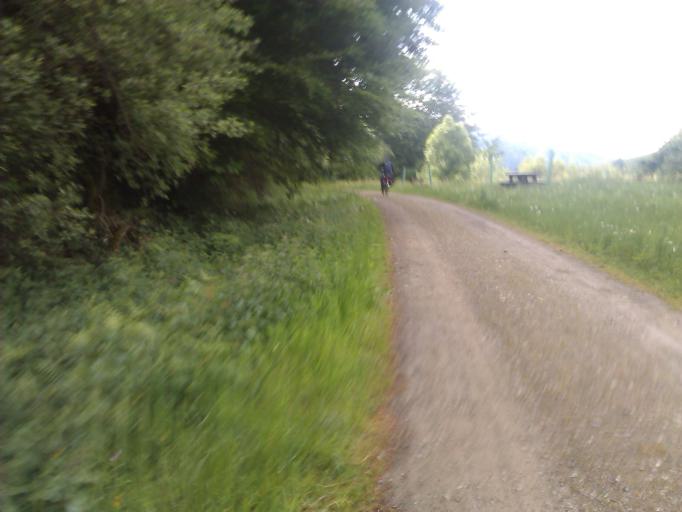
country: ES
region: Navarre
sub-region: Provincia de Navarra
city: Leitza
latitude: 43.0567
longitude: -1.9030
